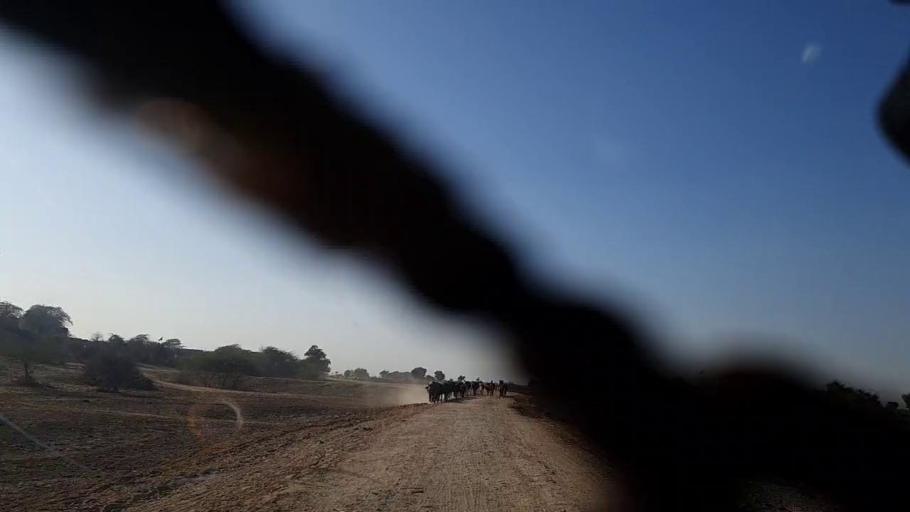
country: PK
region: Sindh
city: Khanpur
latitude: 27.7693
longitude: 69.2927
